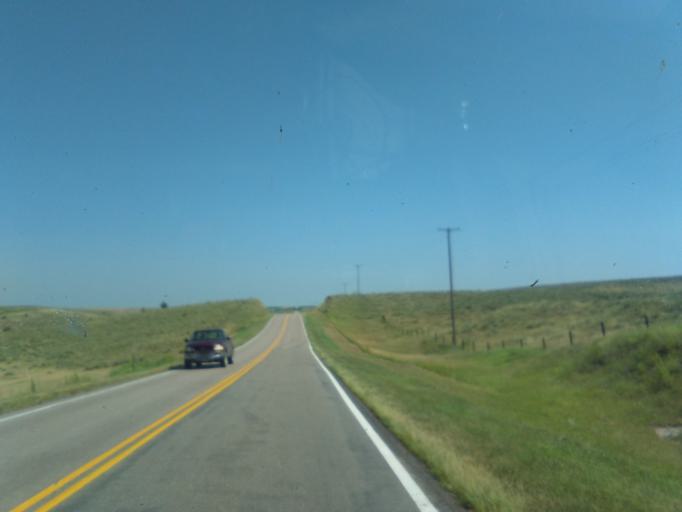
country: US
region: Nebraska
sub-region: Dundy County
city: Benkelman
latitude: 39.8683
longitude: -101.5412
